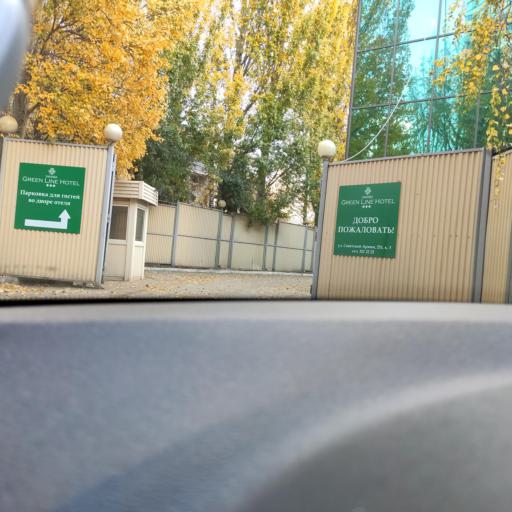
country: RU
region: Samara
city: Samara
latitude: 53.2374
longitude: 50.1830
